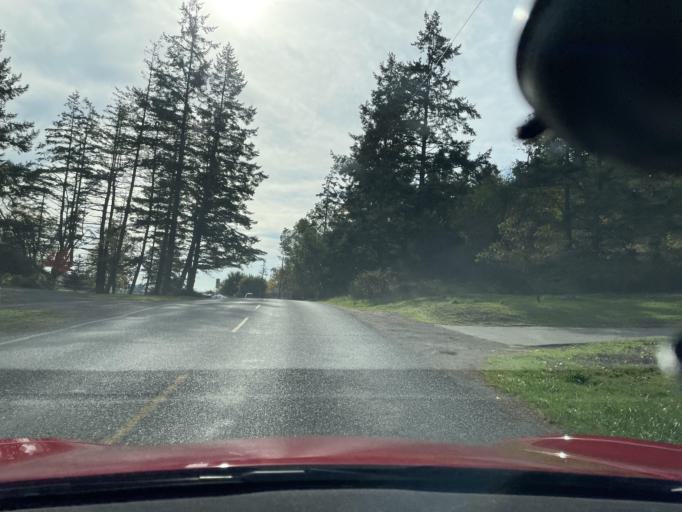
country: US
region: Washington
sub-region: San Juan County
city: Friday Harbor
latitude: 48.5332
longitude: -123.0269
